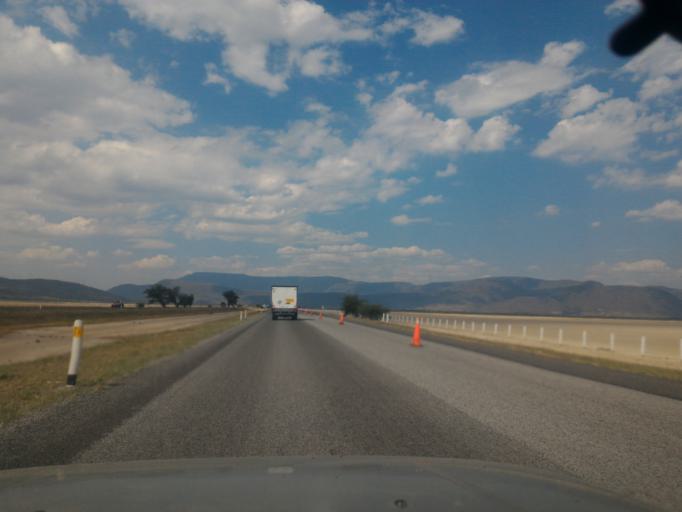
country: MX
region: Jalisco
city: Atoyac
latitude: 20.1122
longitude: -103.5112
